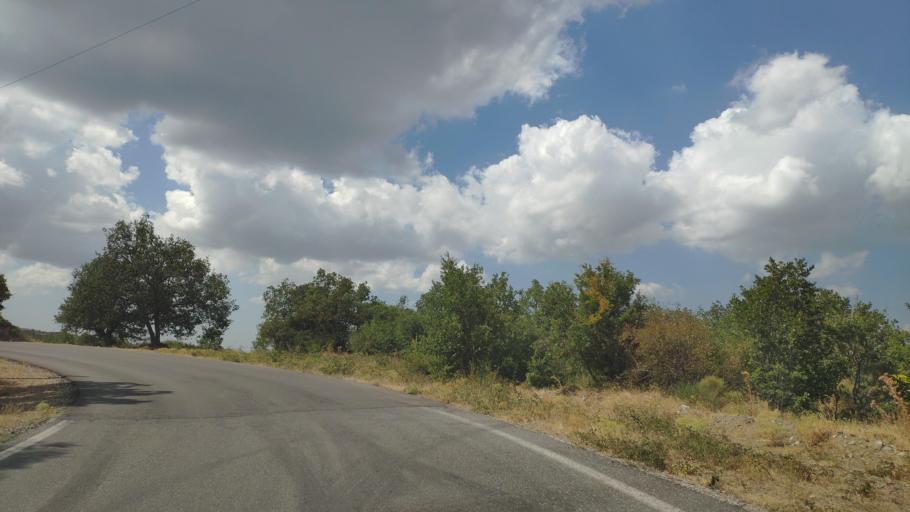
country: GR
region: Peloponnese
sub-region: Nomos Lakonias
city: Kariai
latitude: 37.2768
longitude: 22.5168
